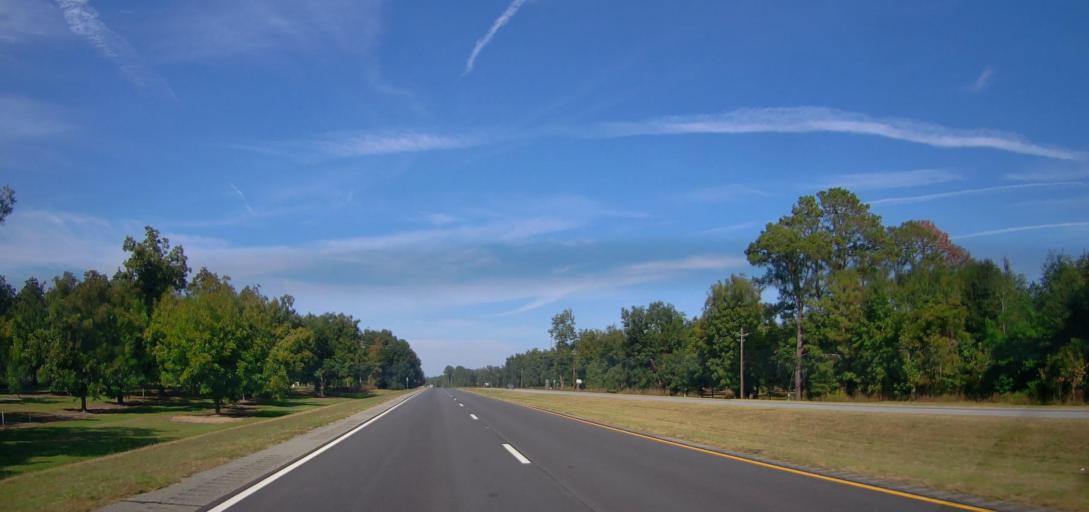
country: US
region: Georgia
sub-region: Dougherty County
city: Putney
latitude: 31.3866
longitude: -84.1484
